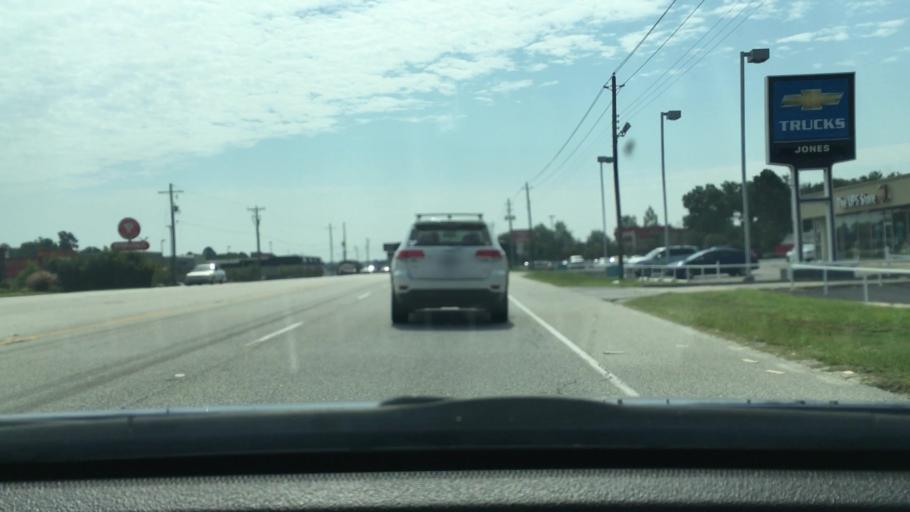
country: US
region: South Carolina
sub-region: Sumter County
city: Sumter
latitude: 33.9563
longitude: -80.3835
